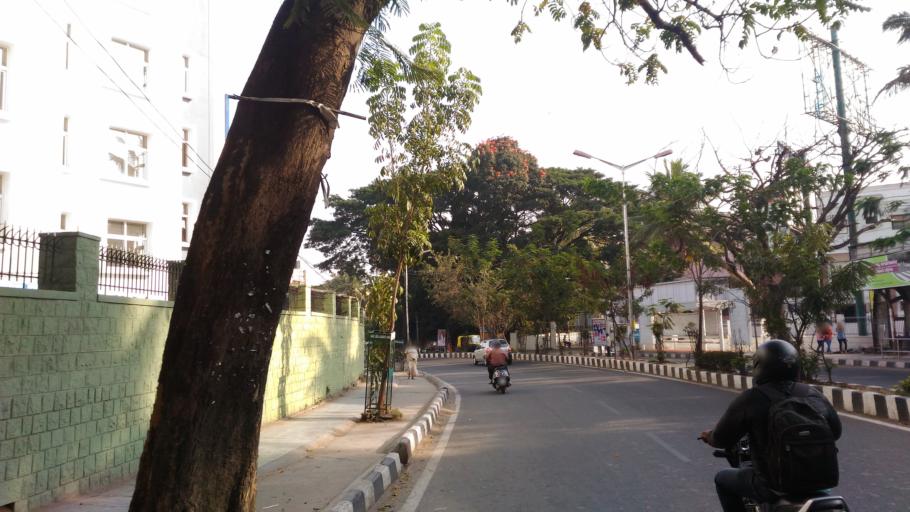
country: IN
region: Karnataka
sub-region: Bangalore Urban
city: Bangalore
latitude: 12.9285
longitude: 77.5875
